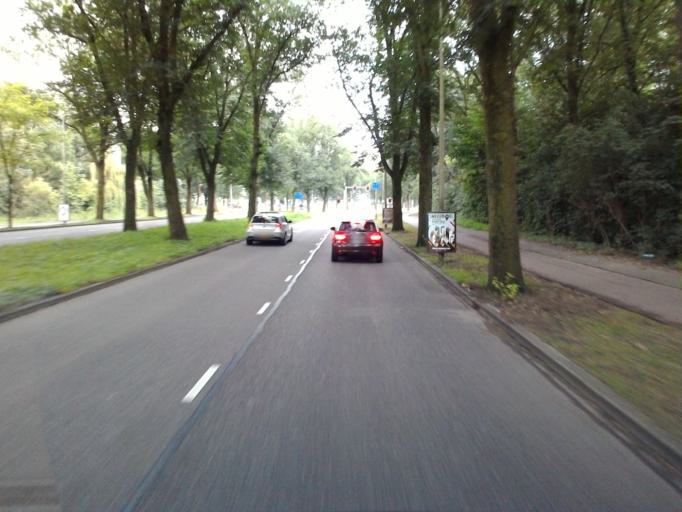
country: NL
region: Utrecht
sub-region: Gemeente Utrecht
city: Utrecht
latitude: 52.1116
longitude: 5.1092
